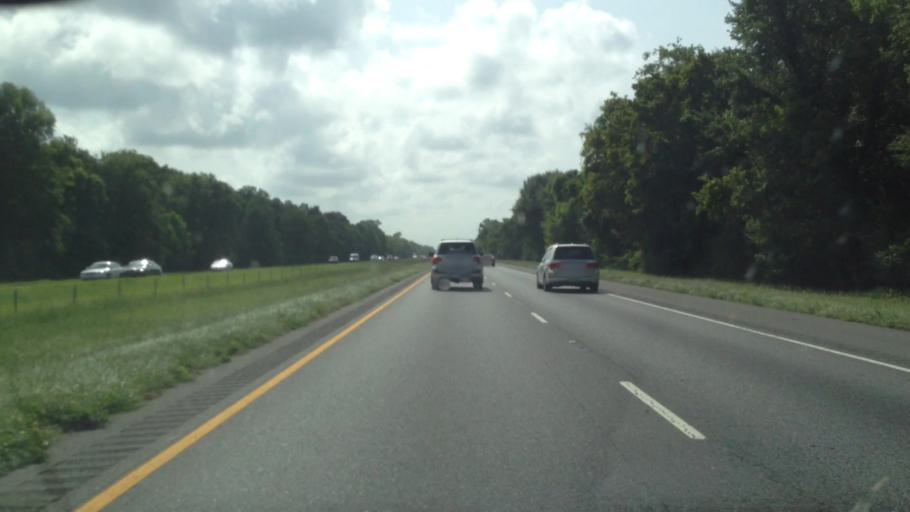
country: US
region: Louisiana
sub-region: Ascension Parish
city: Sorrento
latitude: 30.1614
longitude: -90.8400
